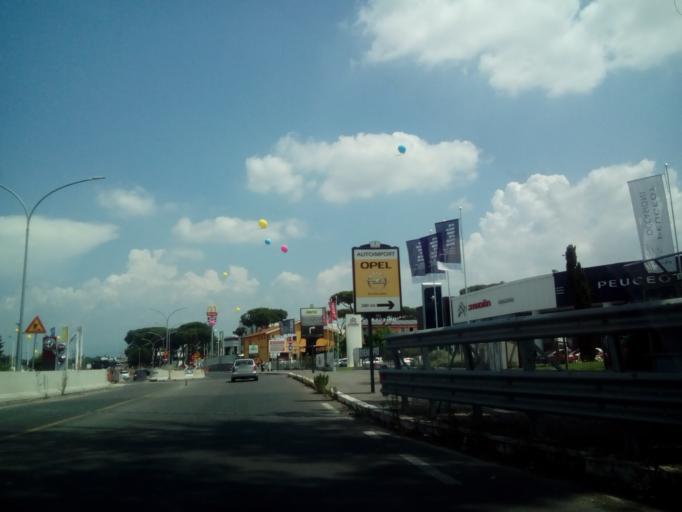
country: IT
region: Latium
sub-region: Citta metropolitana di Roma Capitale
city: Colle Verde
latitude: 41.9327
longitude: 12.5934
